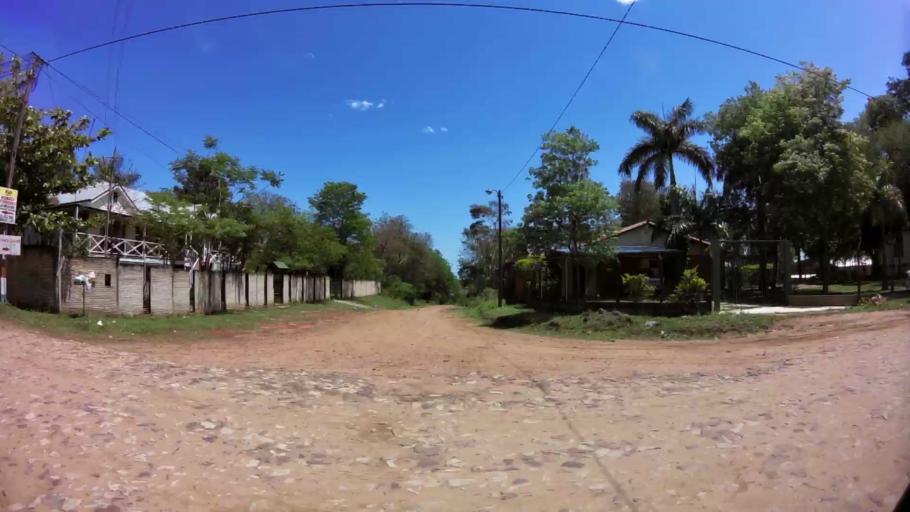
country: PY
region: Central
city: Colonia Mariano Roque Alonso
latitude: -25.1993
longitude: -57.5508
